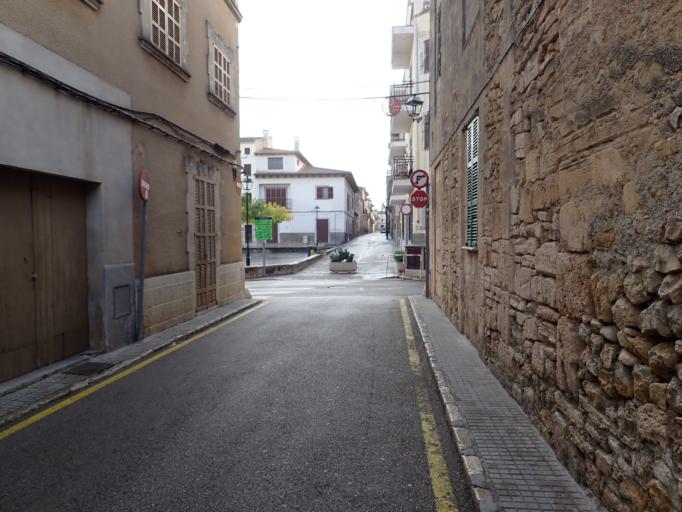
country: ES
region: Balearic Islands
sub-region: Illes Balears
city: Petra
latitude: 39.6148
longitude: 3.1119
